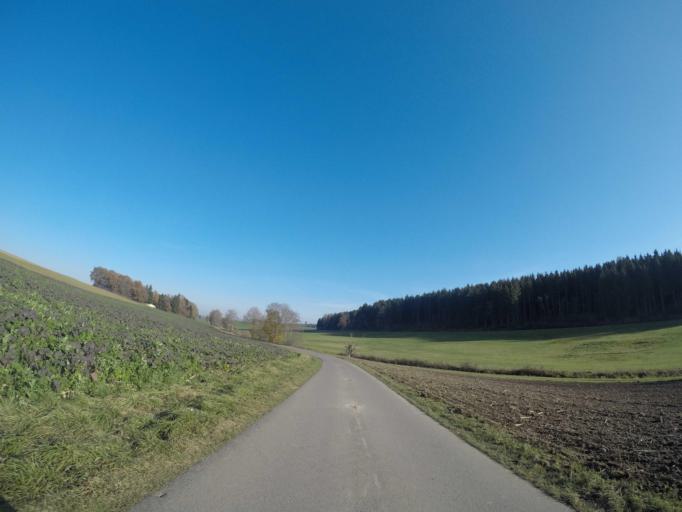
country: DE
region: Baden-Wuerttemberg
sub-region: Tuebingen Region
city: Unterwachingen
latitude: 48.1880
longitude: 9.6452
